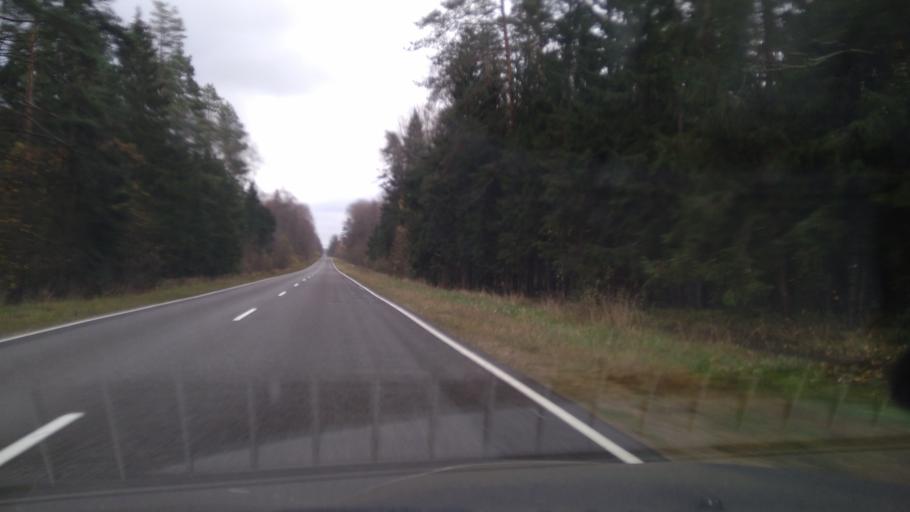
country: BY
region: Minsk
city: Urechcha
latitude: 53.2123
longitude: 27.8799
